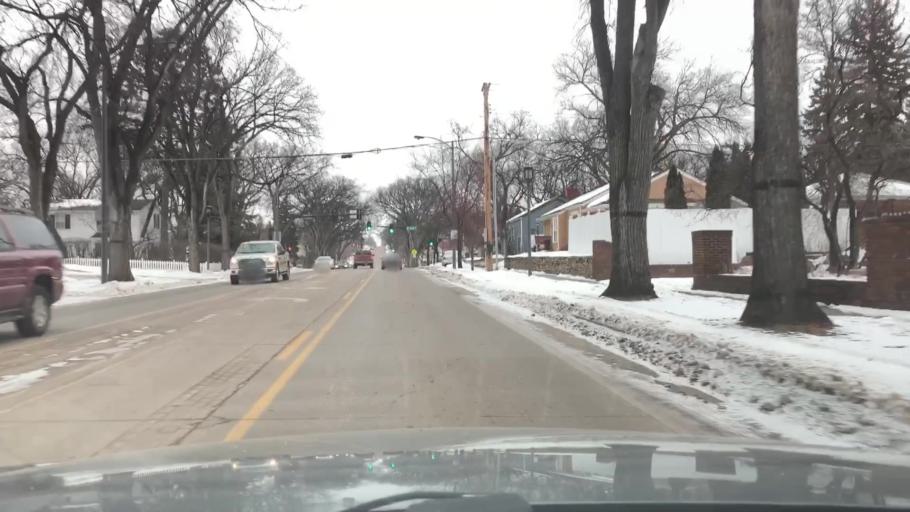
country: US
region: North Dakota
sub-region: Burleigh County
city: Bismarck
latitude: 46.8109
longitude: -100.7943
